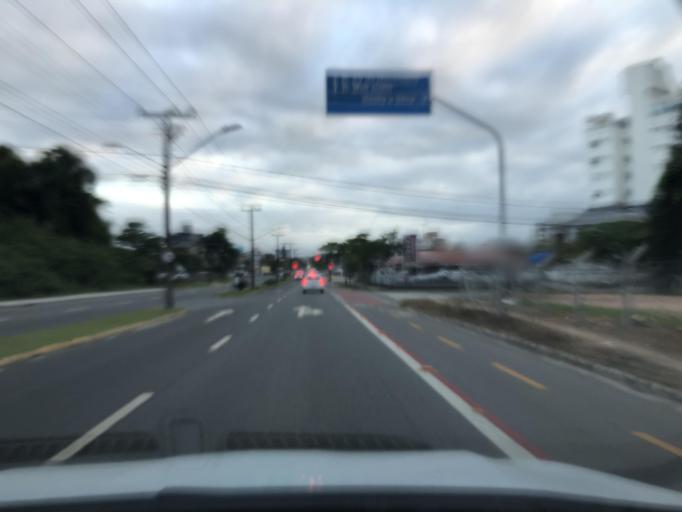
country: BR
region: Santa Catarina
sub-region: Joinville
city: Joinville
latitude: -26.2655
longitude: -48.8620
